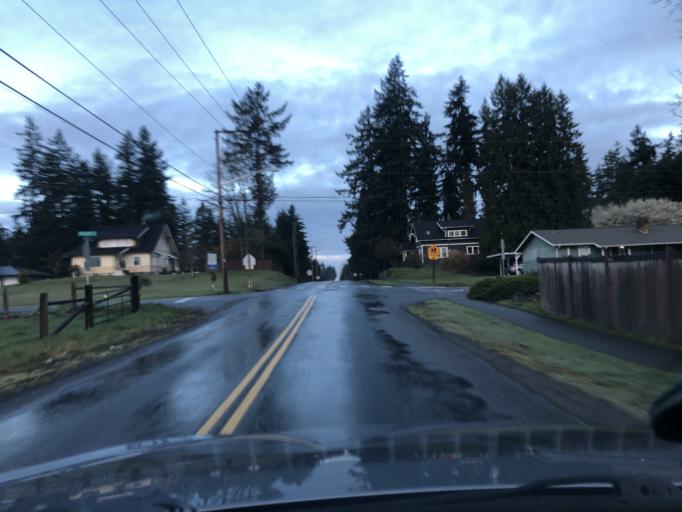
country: US
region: Washington
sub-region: Pierce County
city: North Puyallup
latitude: 47.2248
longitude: -122.2776
